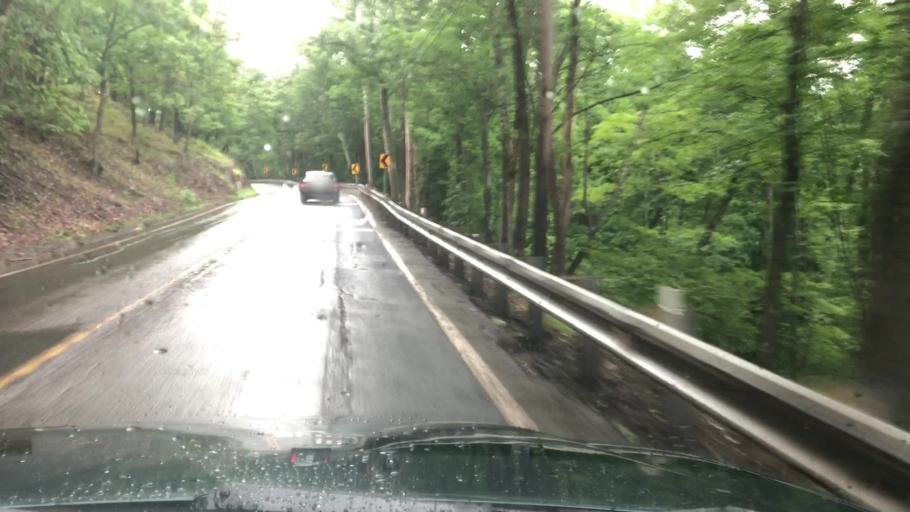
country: US
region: Pennsylvania
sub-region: Monroe County
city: Mountainhome
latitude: 41.2422
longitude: -75.2307
